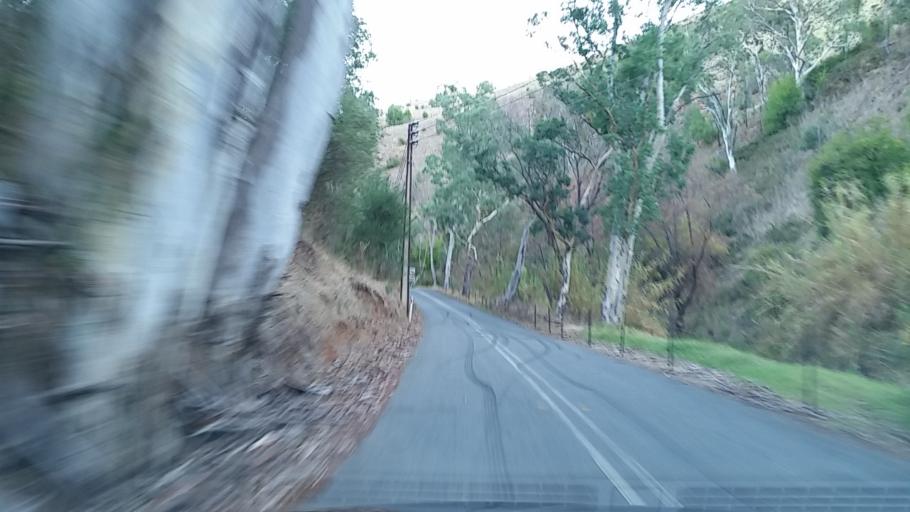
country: AU
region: South Australia
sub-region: Campbelltown
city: Athelstone
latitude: -34.8696
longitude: 138.7527
